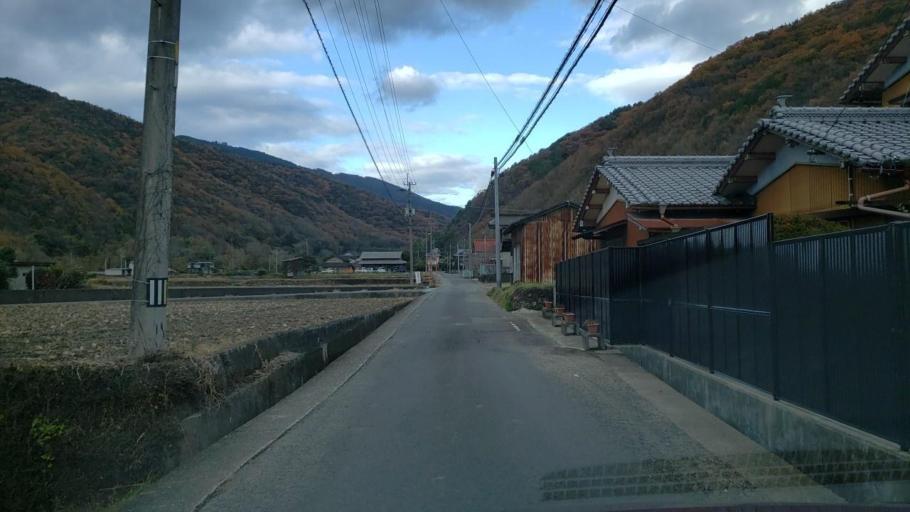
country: JP
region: Tokushima
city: Wakimachi
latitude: 34.1032
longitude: 134.2250
